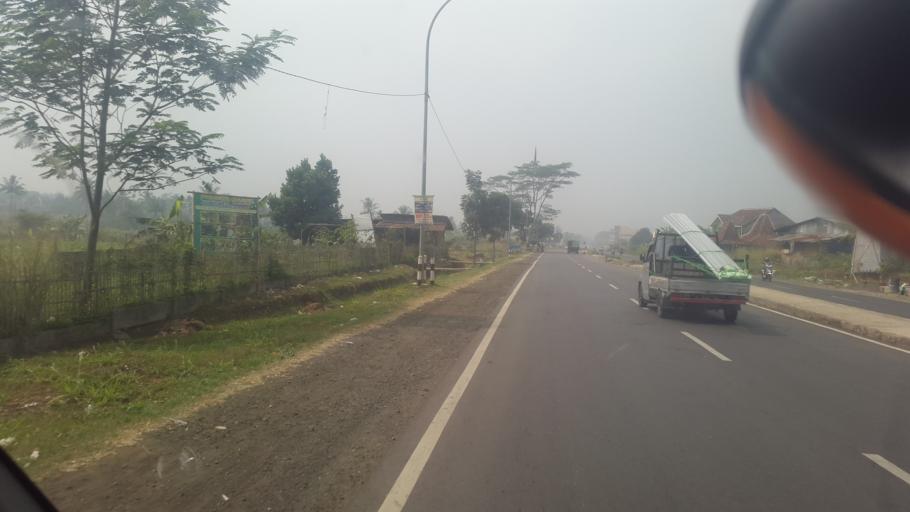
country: ID
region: West Java
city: Sukabumi
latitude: -6.9223
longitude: 106.8916
